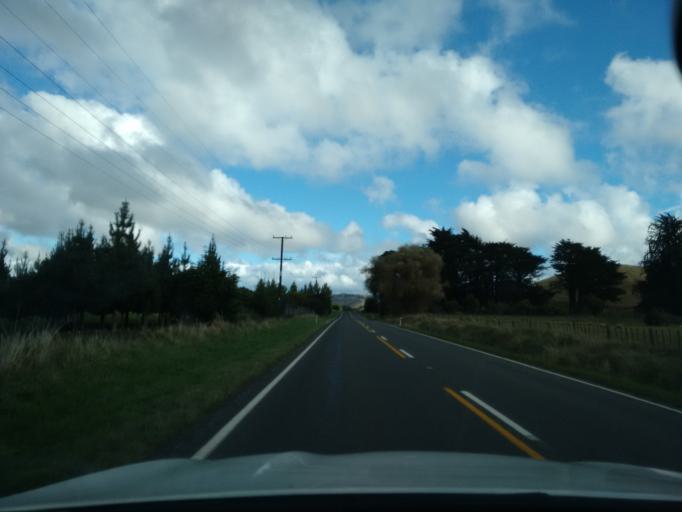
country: NZ
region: Manawatu-Wanganui
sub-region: Ruapehu District
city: Waiouru
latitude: -39.4080
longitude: 175.2848
